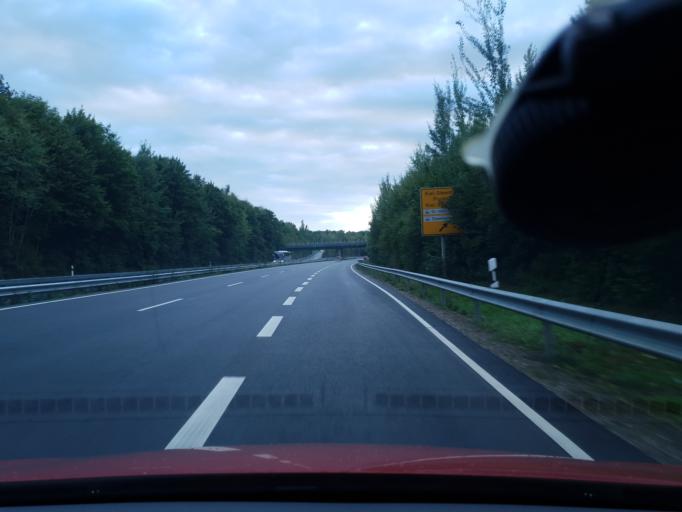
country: DE
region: Schleswig-Holstein
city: Kronshagen
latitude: 54.3547
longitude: 10.0985
